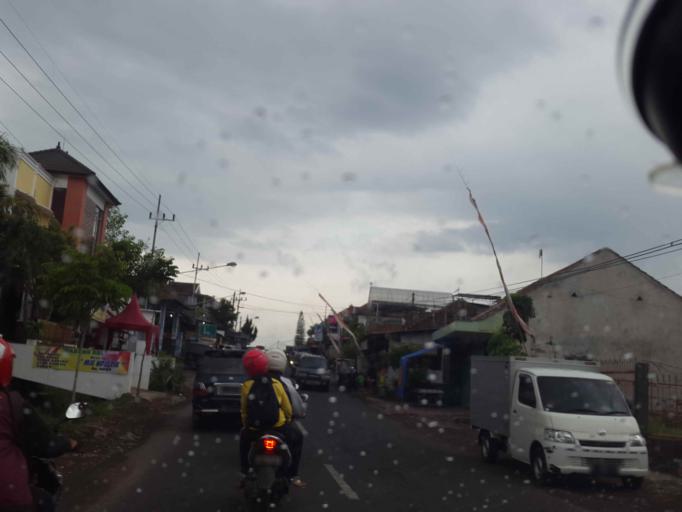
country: ID
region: East Java
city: Batu
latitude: -7.8430
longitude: 112.5281
